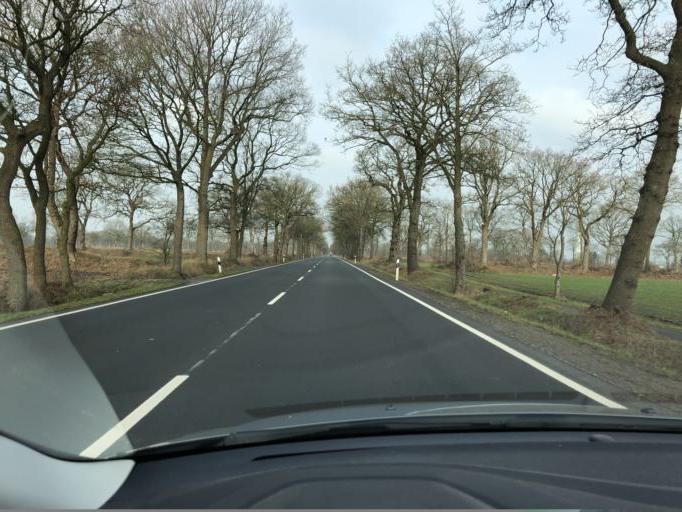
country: DE
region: Lower Saxony
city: Mittegrossefehn
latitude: 53.3597
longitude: 7.5968
